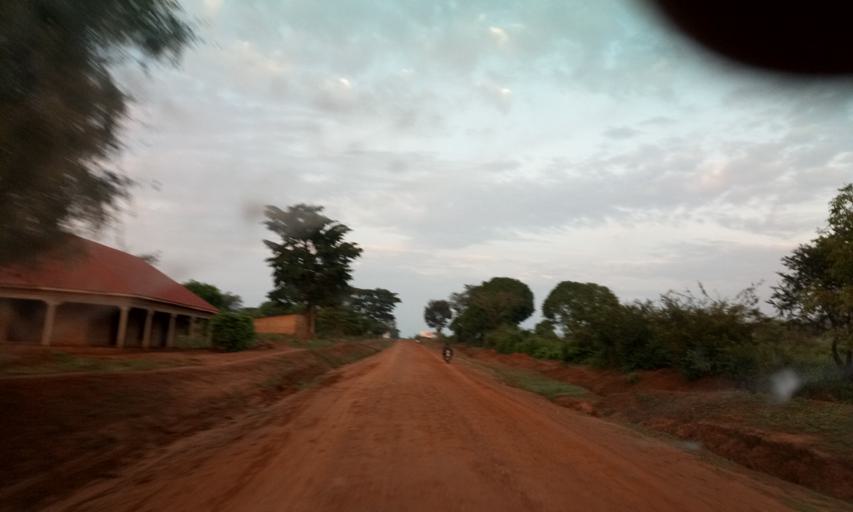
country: UG
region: Eastern Region
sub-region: Ngora District
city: Ngora
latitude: 1.4665
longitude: 33.8043
